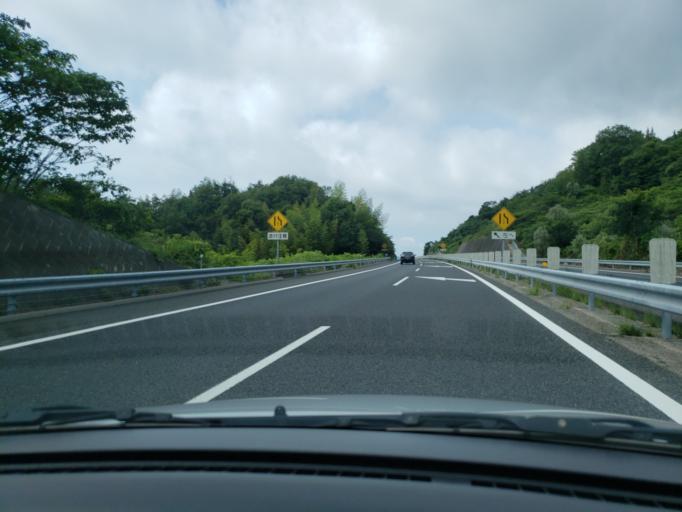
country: JP
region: Hiroshima
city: Innoshima
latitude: 34.2800
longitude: 133.1096
